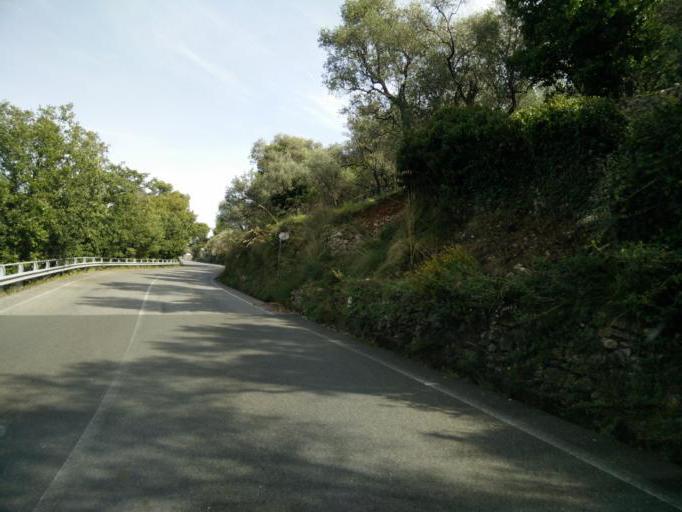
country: IT
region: Liguria
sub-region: Provincia di La Spezia
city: Le Grazie
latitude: 44.0610
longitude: 9.8399
